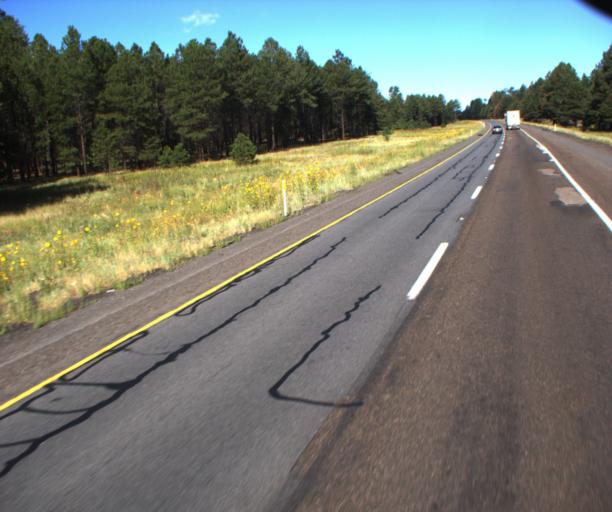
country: US
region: Arizona
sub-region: Coconino County
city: Parks
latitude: 35.2484
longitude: -111.8512
